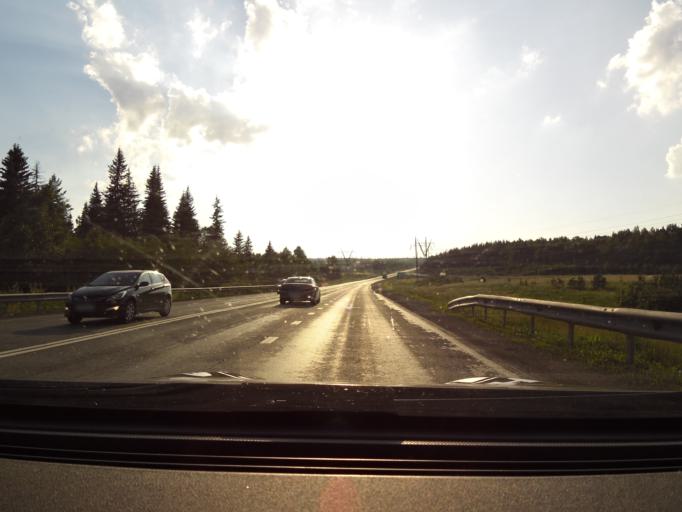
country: RU
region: Sverdlovsk
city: Revda
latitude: 56.8269
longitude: 59.8683
